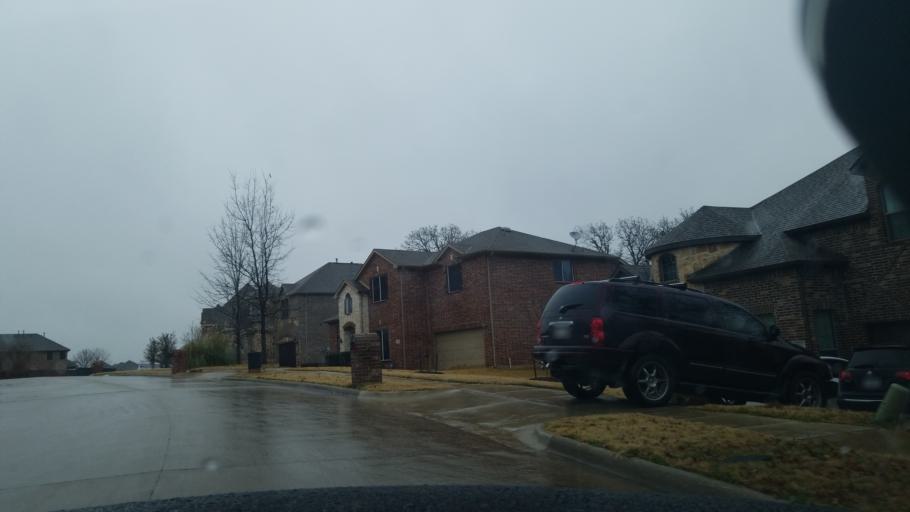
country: US
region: Texas
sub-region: Denton County
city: Corinth
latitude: 33.1352
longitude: -97.0917
